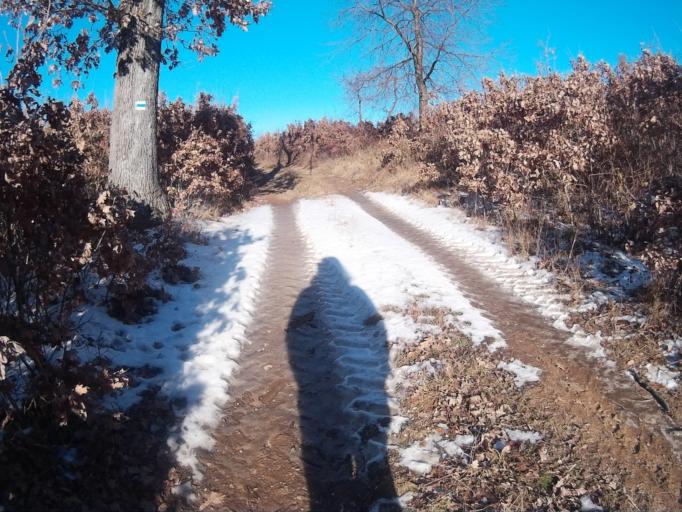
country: HU
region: Borsod-Abauj-Zemplen
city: Putnok
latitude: 48.4134
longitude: 20.4811
